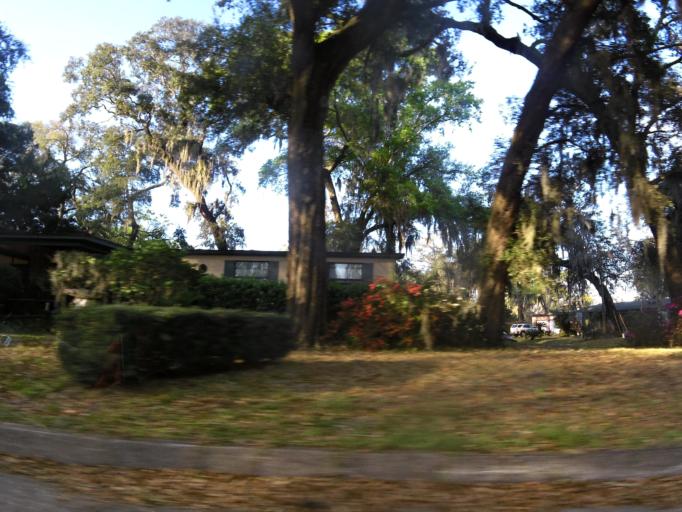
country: US
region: Florida
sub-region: Duval County
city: Jacksonville
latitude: 30.4397
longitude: -81.6379
